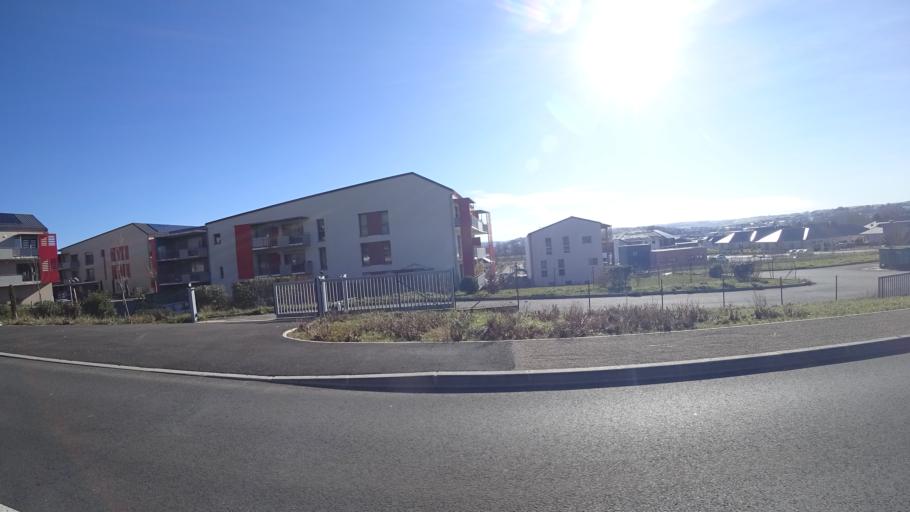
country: FR
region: Midi-Pyrenees
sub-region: Departement de l'Aveyron
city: Rodez
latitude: 44.3774
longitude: 2.5796
